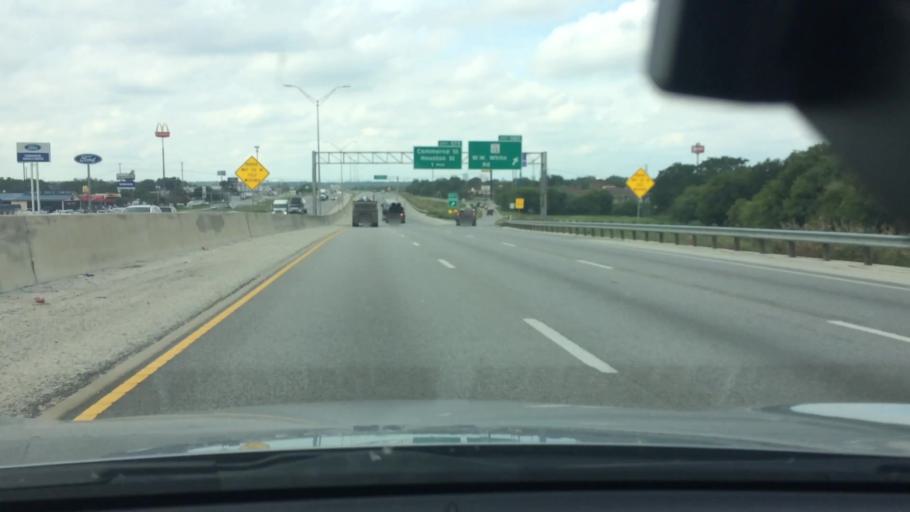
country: US
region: Texas
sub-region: Bexar County
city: Kirby
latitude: 29.4327
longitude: -98.4017
